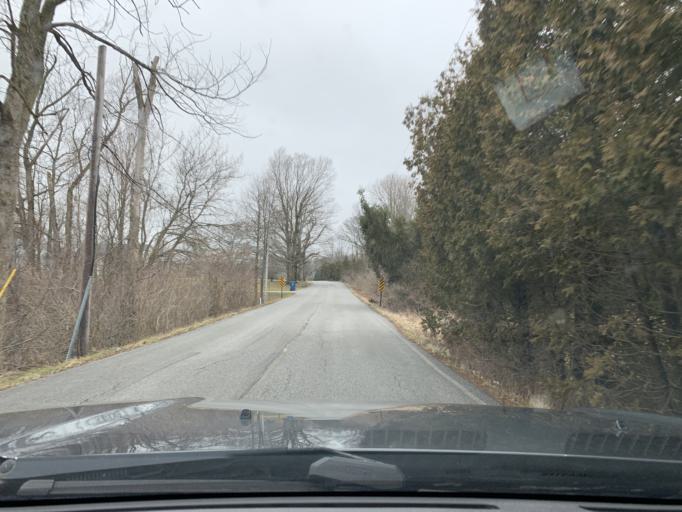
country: US
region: Indiana
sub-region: Porter County
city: Chesterton
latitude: 41.6104
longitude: -87.0098
